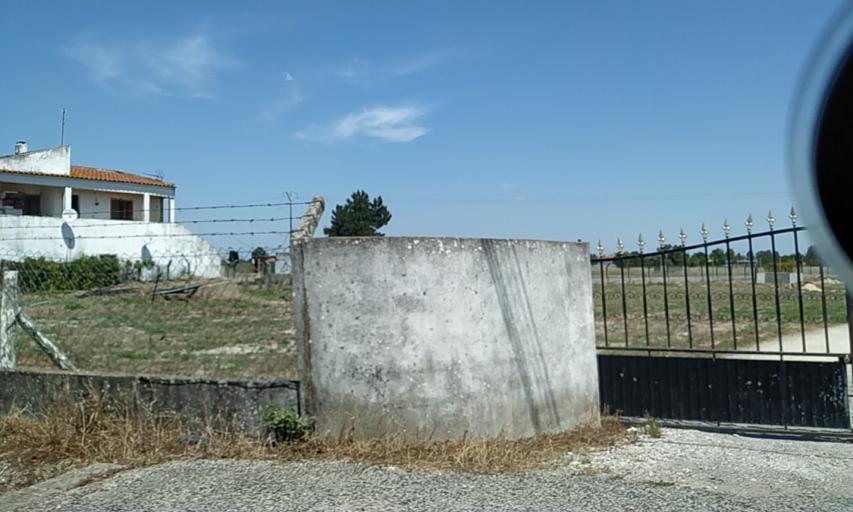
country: PT
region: Setubal
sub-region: Palmela
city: Pinhal Novo
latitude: 38.6422
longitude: -8.7431
